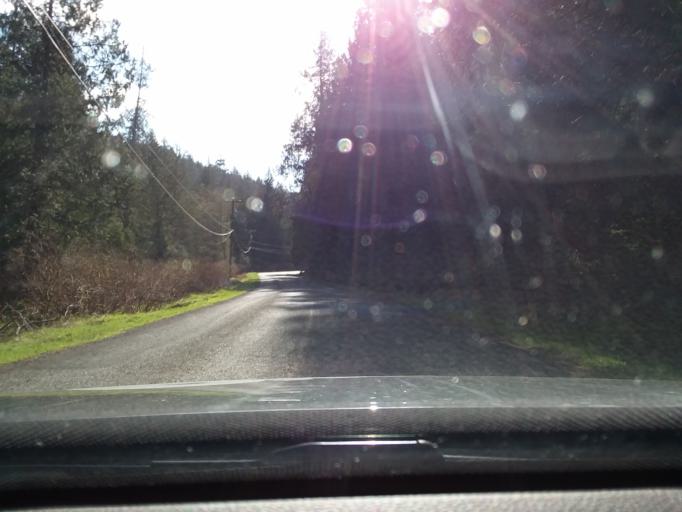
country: CA
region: British Columbia
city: North Cowichan
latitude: 48.9281
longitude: -123.4585
